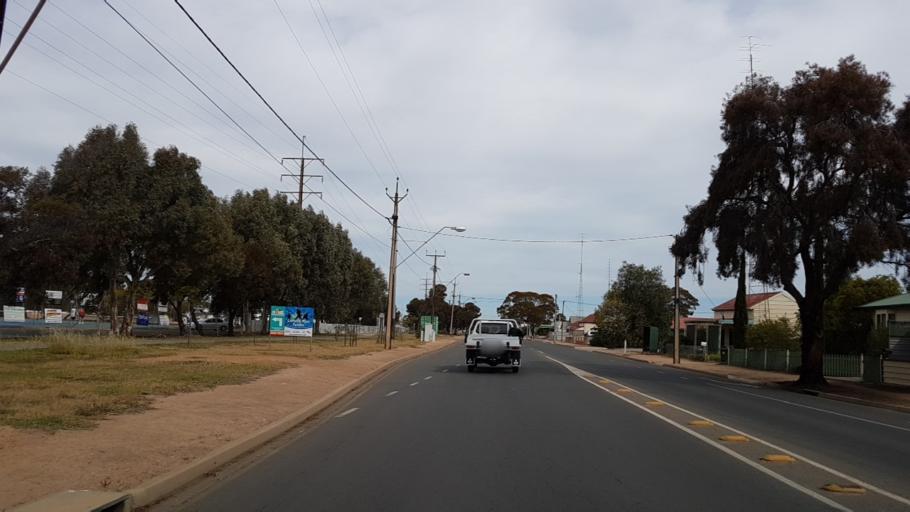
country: AU
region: South Australia
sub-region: Port Pirie City and Dists
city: Port Pirie
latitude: -33.1853
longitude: 138.0039
